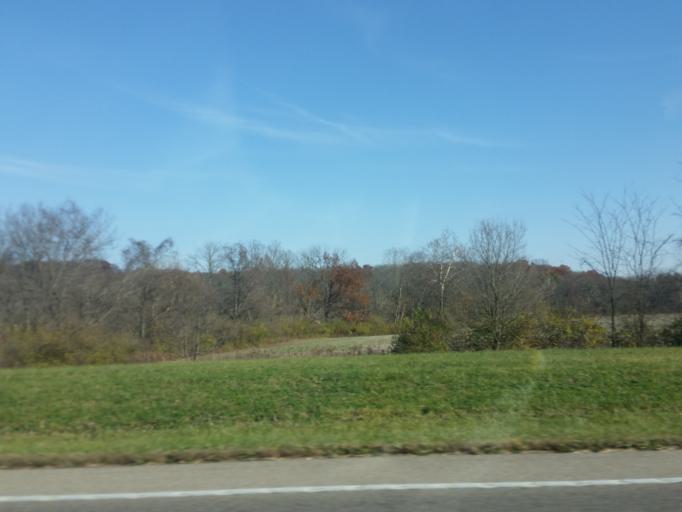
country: US
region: Ohio
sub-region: Butler County
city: Ross
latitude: 39.3365
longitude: -84.6440
